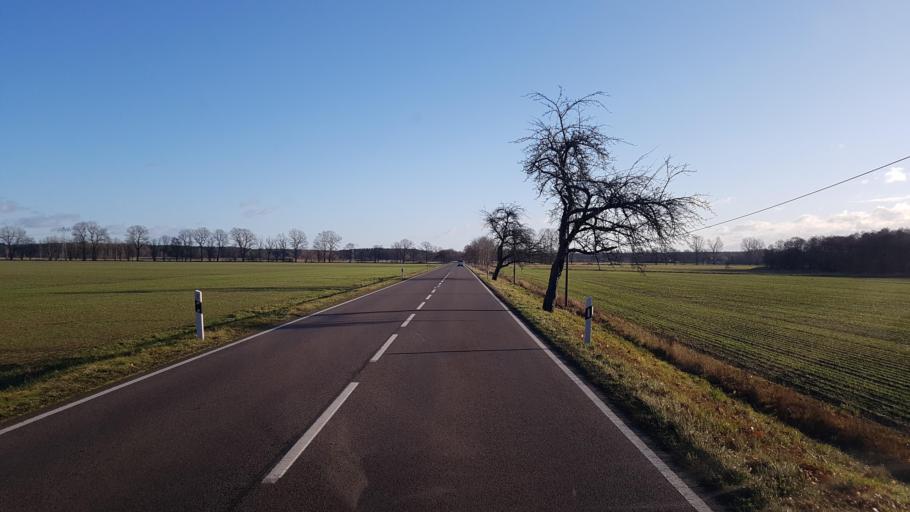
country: DE
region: Brandenburg
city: Heinersbruck
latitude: 51.7291
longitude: 14.4626
